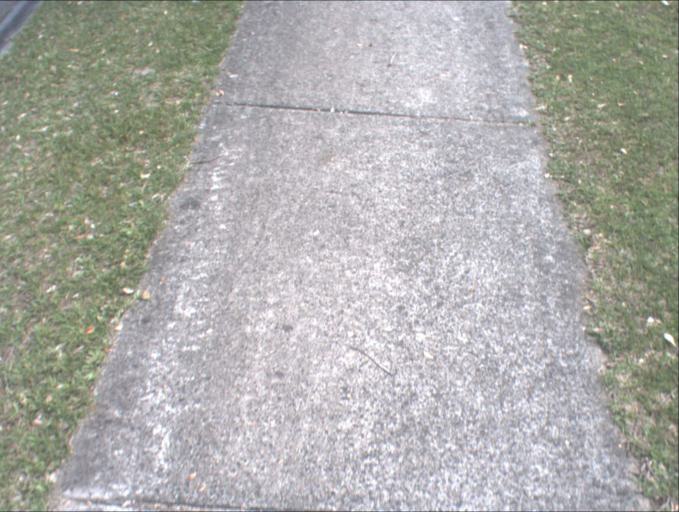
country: AU
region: Queensland
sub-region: Logan
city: Logan Reserve
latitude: -27.6903
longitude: 153.0838
